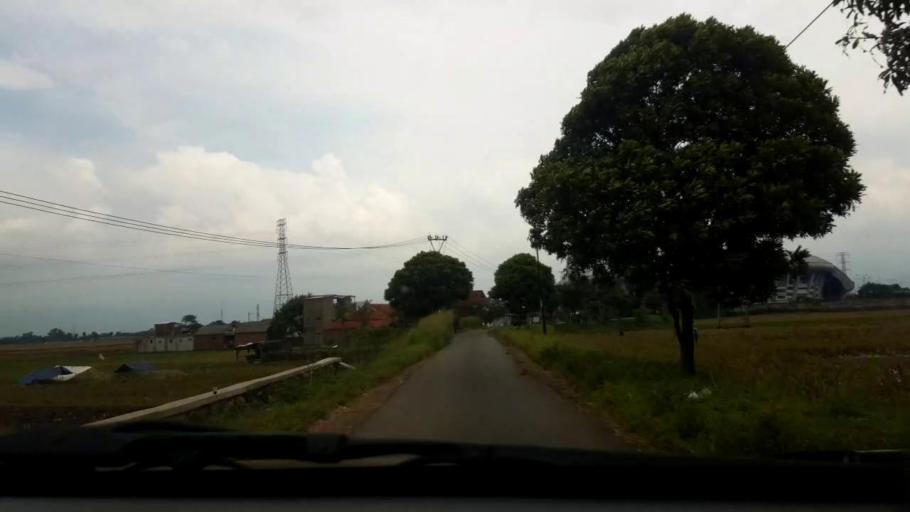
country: ID
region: West Java
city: Cileunyi
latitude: -6.9517
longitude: 107.7129
